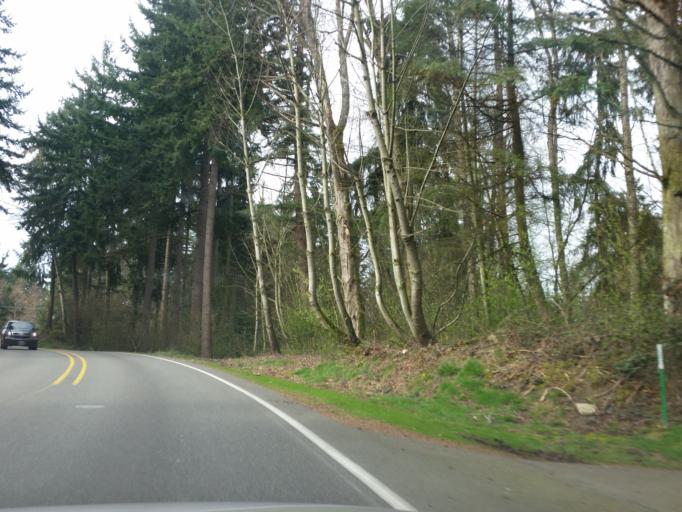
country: US
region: Washington
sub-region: Pierce County
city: McMillin
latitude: 47.1458
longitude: -122.2514
